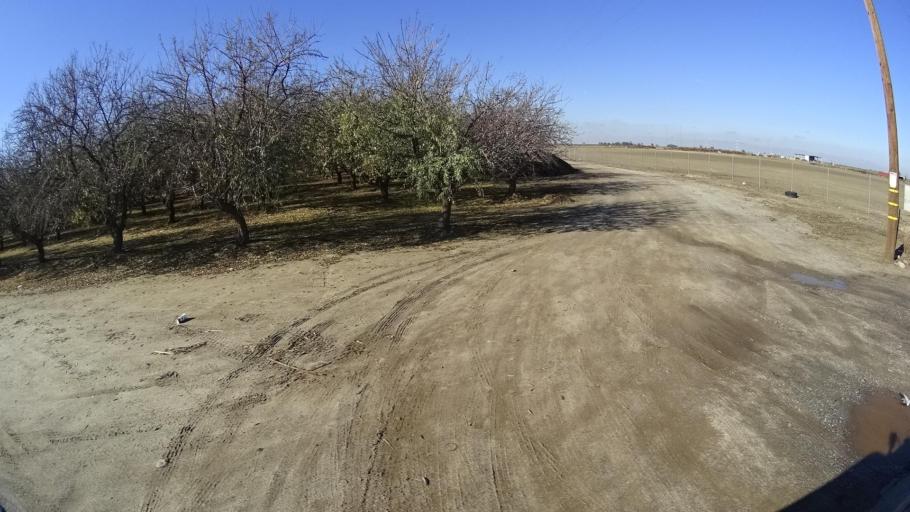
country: US
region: California
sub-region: Kern County
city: Delano
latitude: 35.7396
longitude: -119.2584
